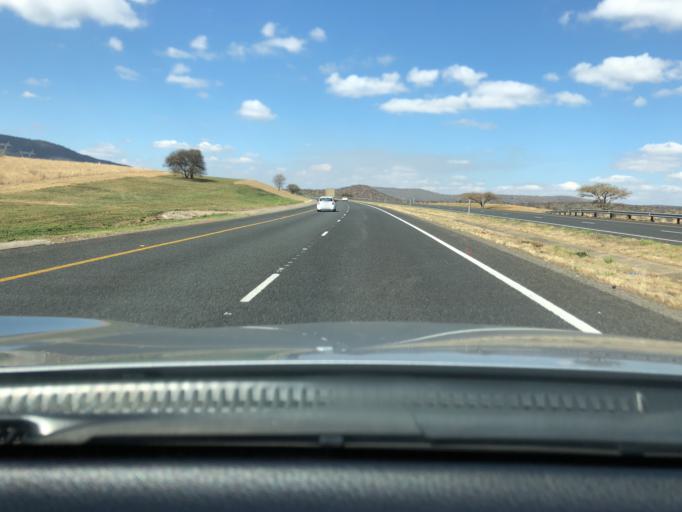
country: ZA
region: KwaZulu-Natal
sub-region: uThukela District Municipality
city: Ladysmith
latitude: -28.7012
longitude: 29.6400
